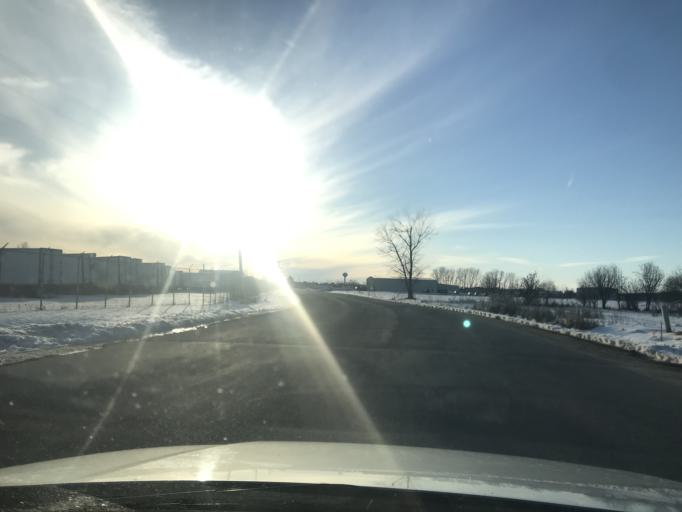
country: US
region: Wisconsin
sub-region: Marinette County
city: Peshtigo
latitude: 45.0579
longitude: -87.7209
